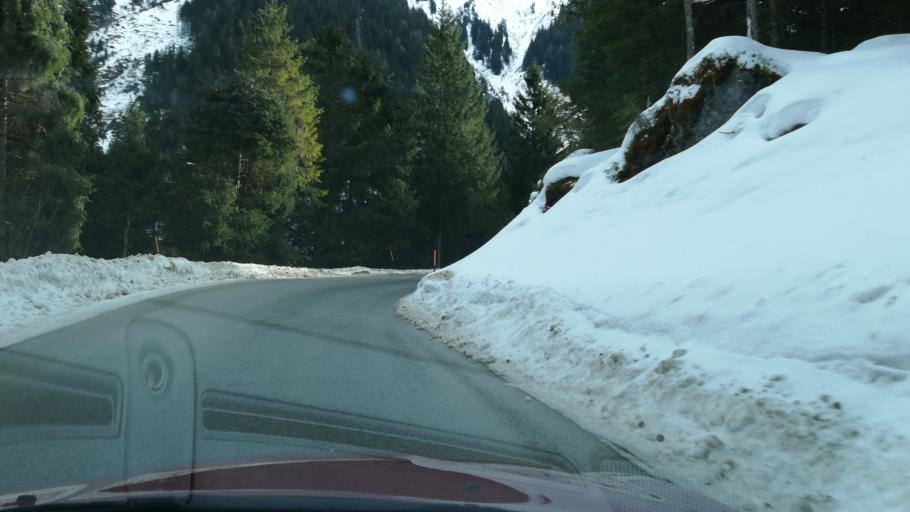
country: AT
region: Styria
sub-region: Politischer Bezirk Liezen
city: Donnersbach
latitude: 47.4203
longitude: 14.1689
